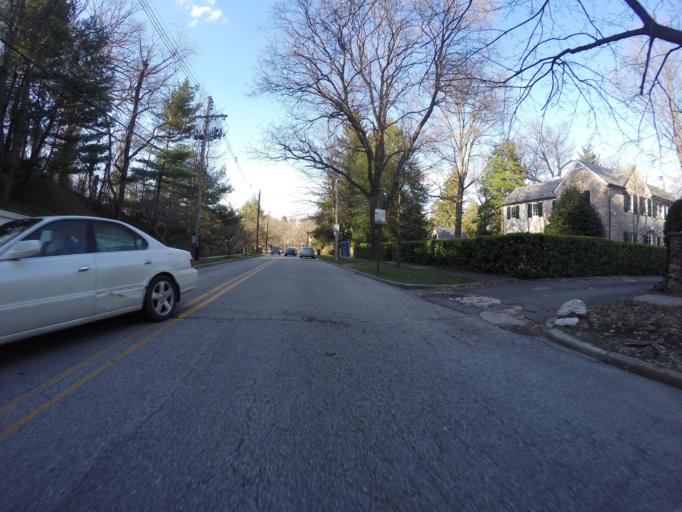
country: US
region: Maryland
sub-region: City of Baltimore
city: Baltimore
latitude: 39.3370
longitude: -76.6284
